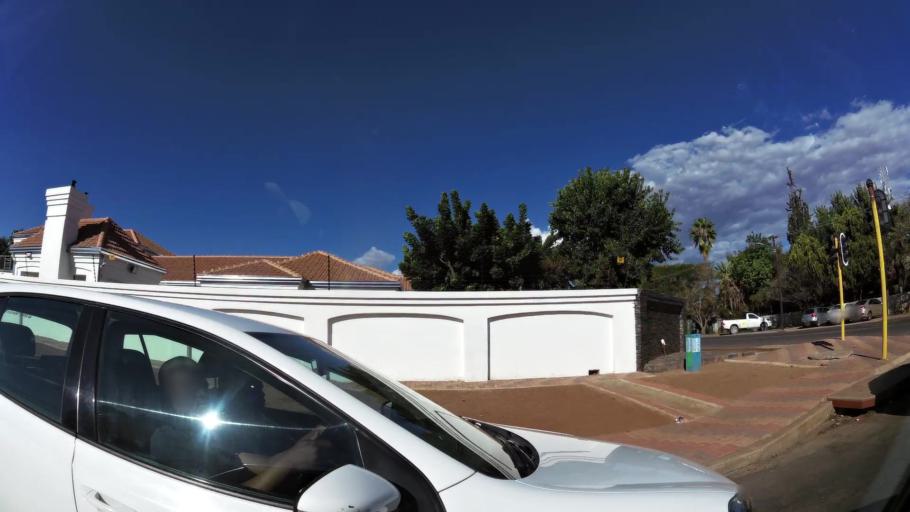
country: ZA
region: Limpopo
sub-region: Waterberg District Municipality
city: Mokopane
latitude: -24.1797
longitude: 29.0009
